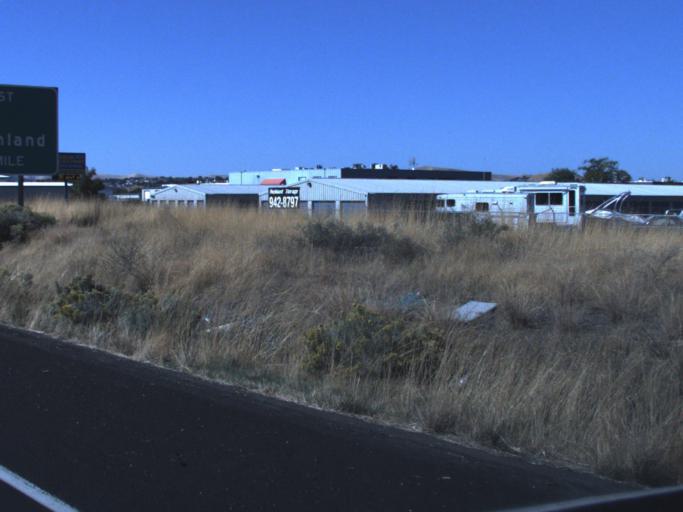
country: US
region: Washington
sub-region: Benton County
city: Richland
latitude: 46.2991
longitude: -119.2988
